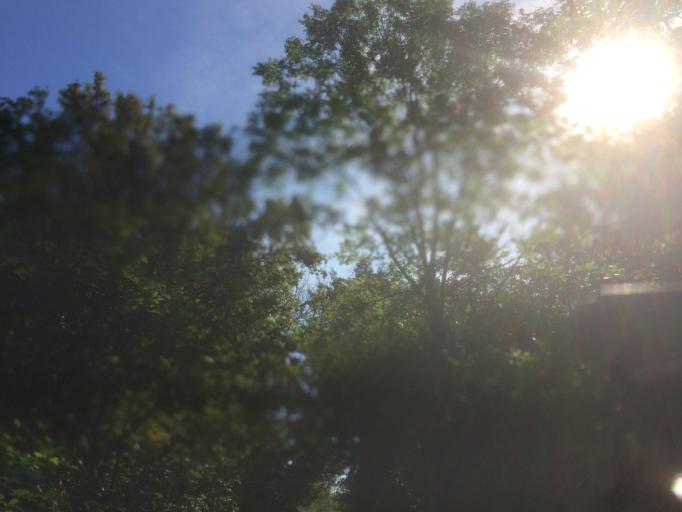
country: GB
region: England
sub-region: Devon
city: Horrabridge
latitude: 50.5201
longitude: -4.1250
